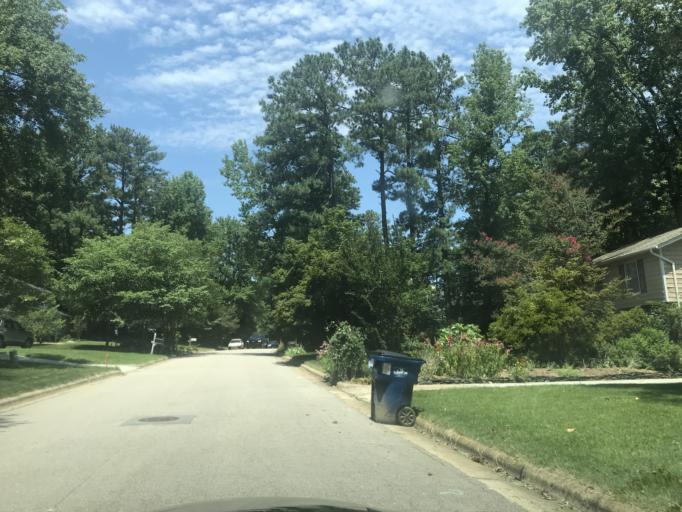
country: US
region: North Carolina
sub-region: Wake County
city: West Raleigh
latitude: 35.8921
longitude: -78.6237
